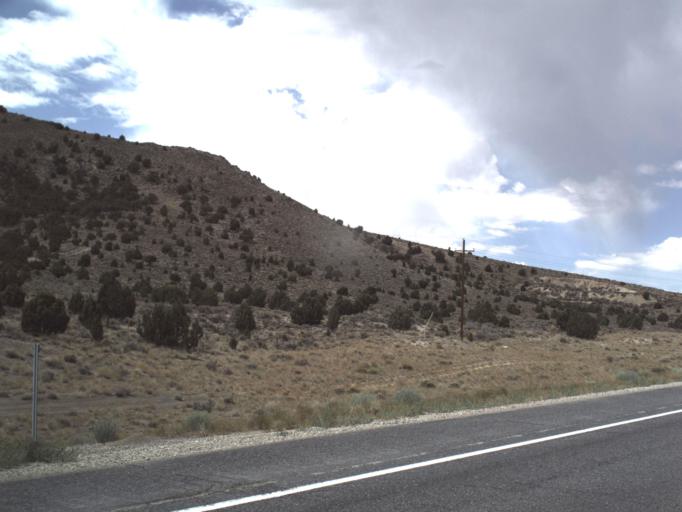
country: US
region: Utah
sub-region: Utah County
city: Eagle Mountain
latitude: 40.0726
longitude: -112.3637
